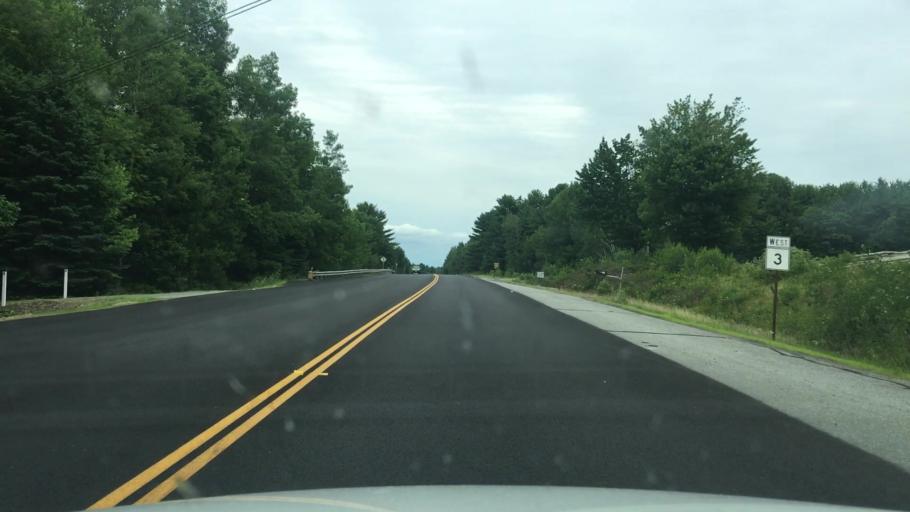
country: US
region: Maine
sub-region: Waldo County
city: Palermo
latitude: 44.3950
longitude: -69.4717
